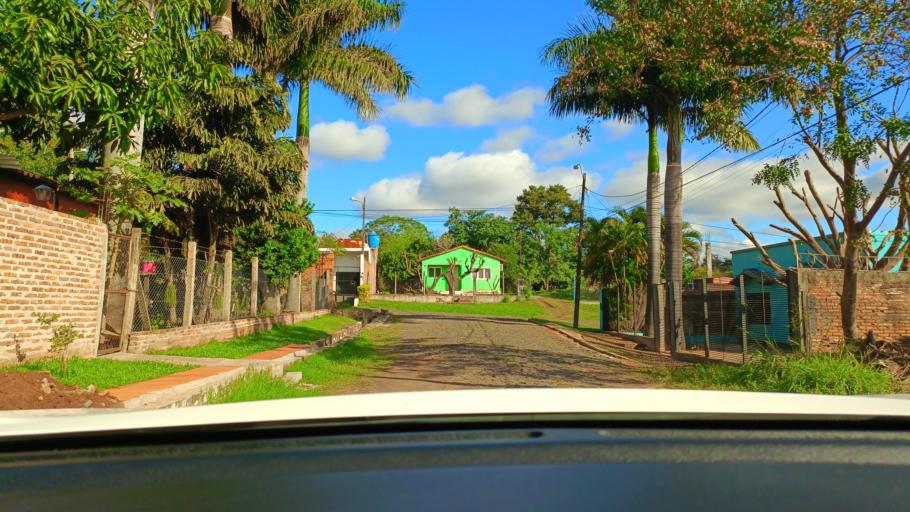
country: PY
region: San Pedro
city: Guayaybi
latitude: -24.6698
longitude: -56.4474
